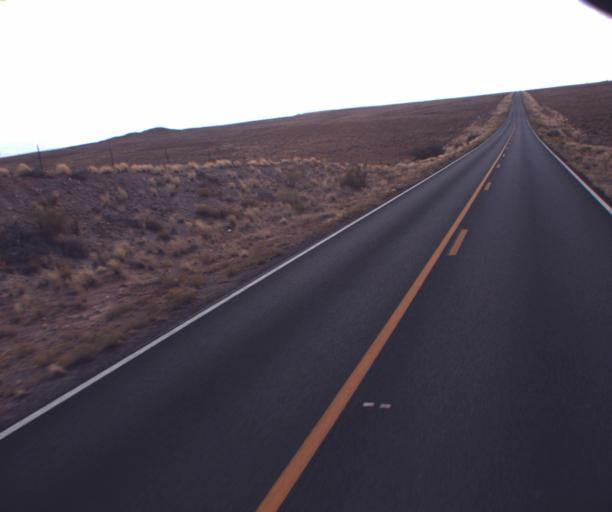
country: US
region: Arizona
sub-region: Apache County
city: Many Farms
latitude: 36.5815
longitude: -109.5554
